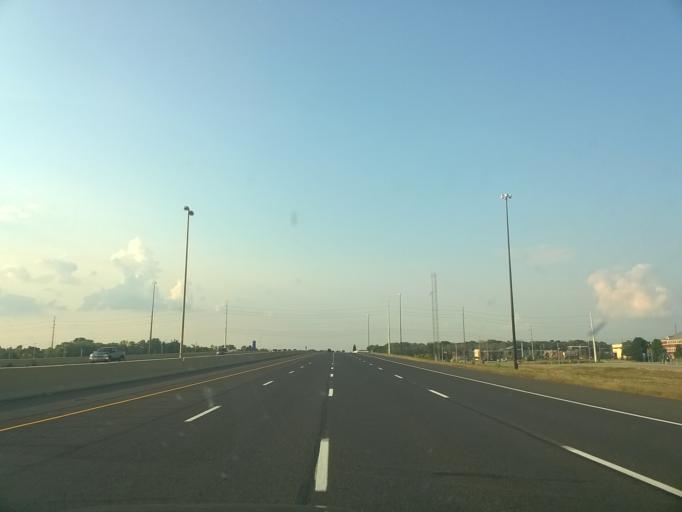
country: US
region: Indiana
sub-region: Boone County
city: Zionsville
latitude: 39.9119
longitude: -86.2695
